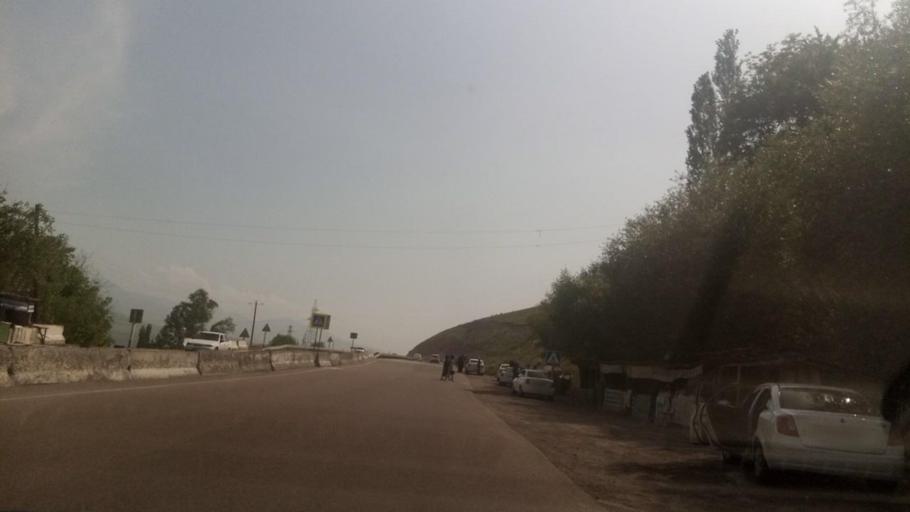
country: UZ
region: Toshkent
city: Angren
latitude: 41.0724
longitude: 70.2336
